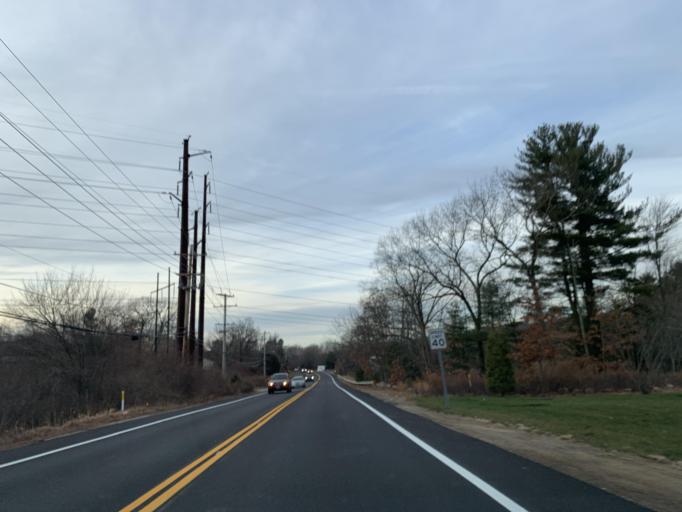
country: US
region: Rhode Island
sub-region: Providence County
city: Johnston
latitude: 41.8534
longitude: -71.5201
